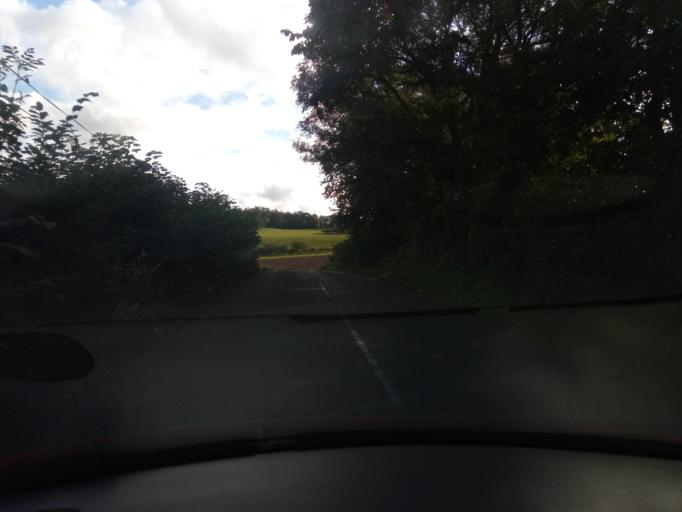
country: GB
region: Scotland
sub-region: The Scottish Borders
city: Coldstream
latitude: 55.5485
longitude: -2.2967
